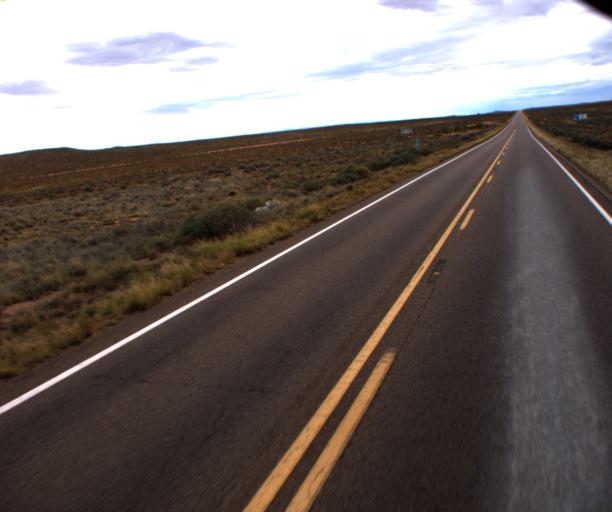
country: US
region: Arizona
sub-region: Navajo County
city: Holbrook
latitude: 34.8258
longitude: -110.1421
